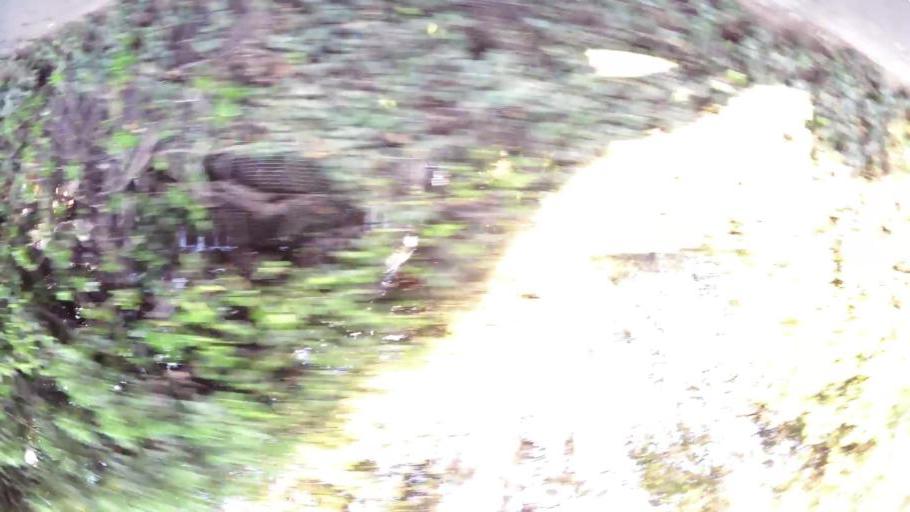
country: CL
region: Santiago Metropolitan
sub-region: Provincia de Santiago
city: Villa Presidente Frei, Nunoa, Santiago, Chile
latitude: -33.4009
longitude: -70.5578
